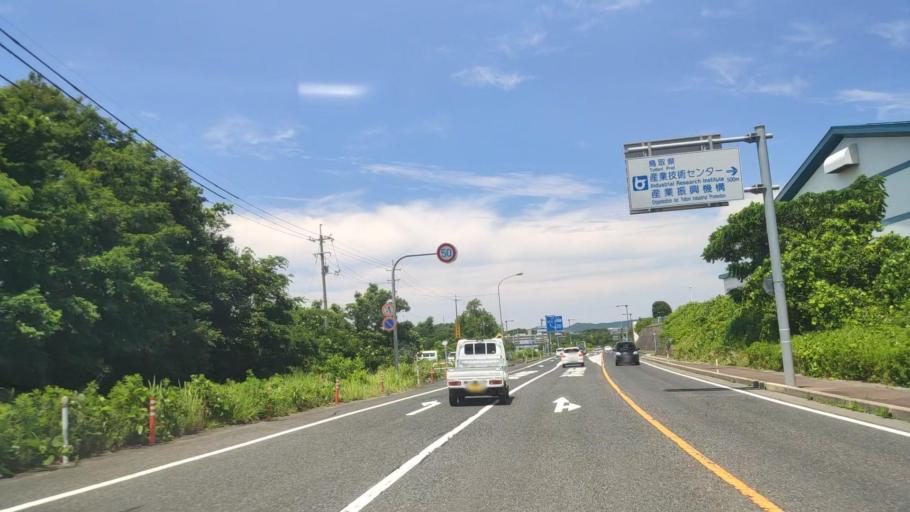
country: JP
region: Tottori
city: Tottori
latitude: 35.4408
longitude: 134.2558
